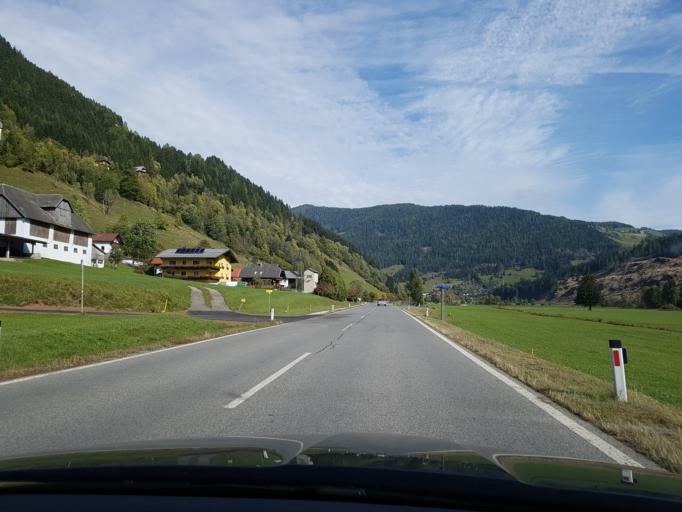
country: AT
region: Carinthia
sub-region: Politischer Bezirk Spittal an der Drau
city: Kleinkirchheim
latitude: 46.8428
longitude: 13.8793
